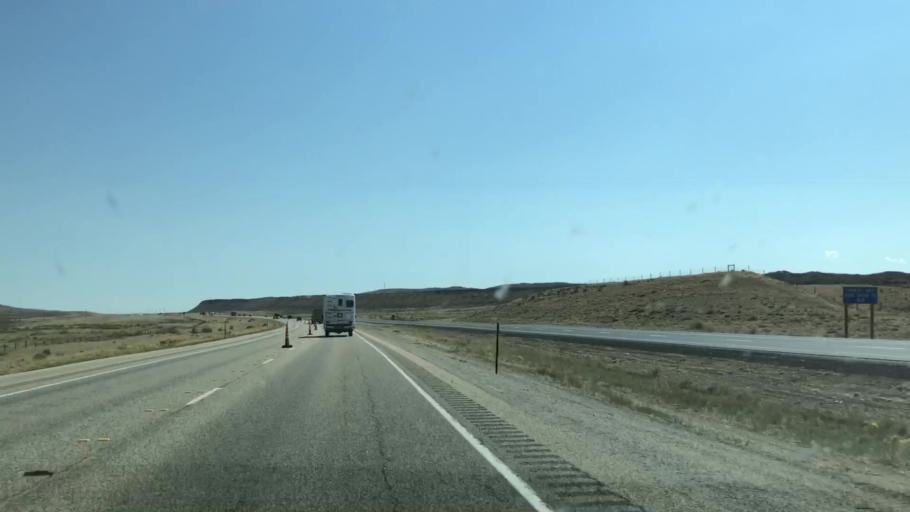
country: US
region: Wyoming
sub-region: Carbon County
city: Rawlins
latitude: 41.7454
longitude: -106.9314
